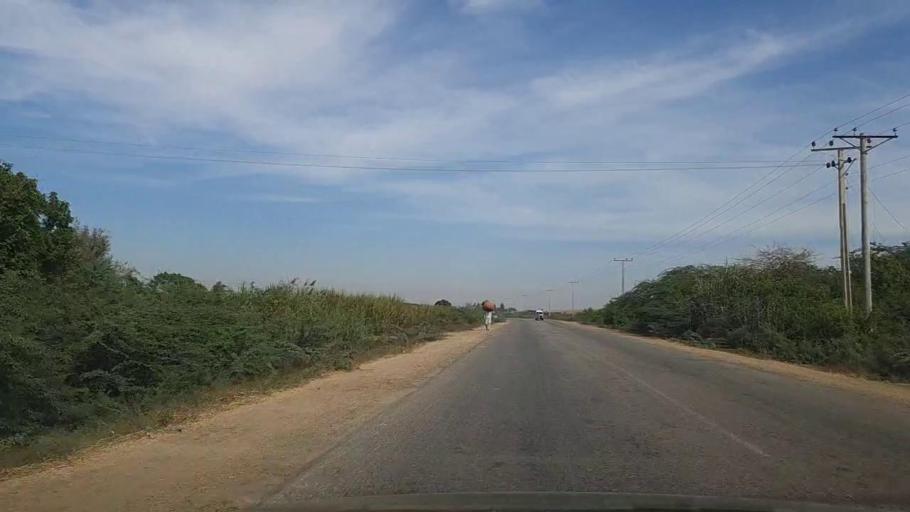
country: PK
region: Sindh
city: Daro Mehar
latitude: 24.9320
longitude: 68.1053
